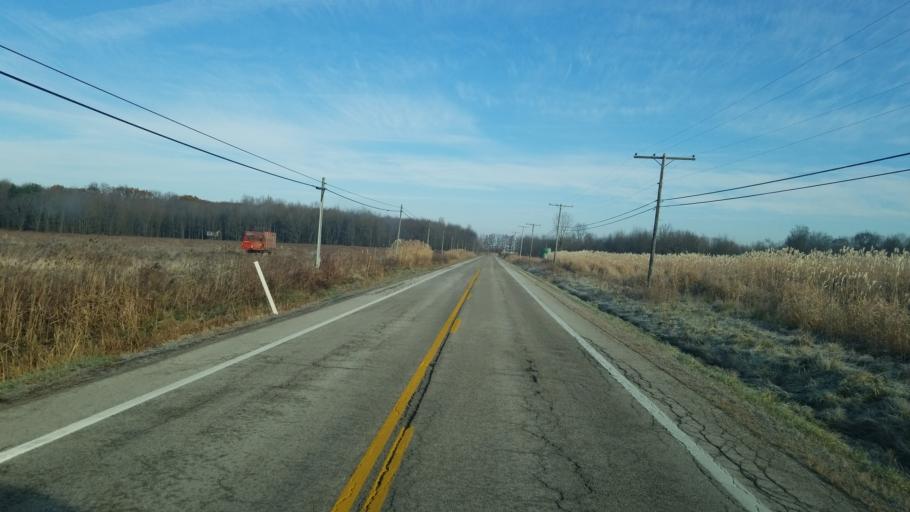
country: US
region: Ohio
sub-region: Ashtabula County
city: Jefferson
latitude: 41.7227
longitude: -80.6690
